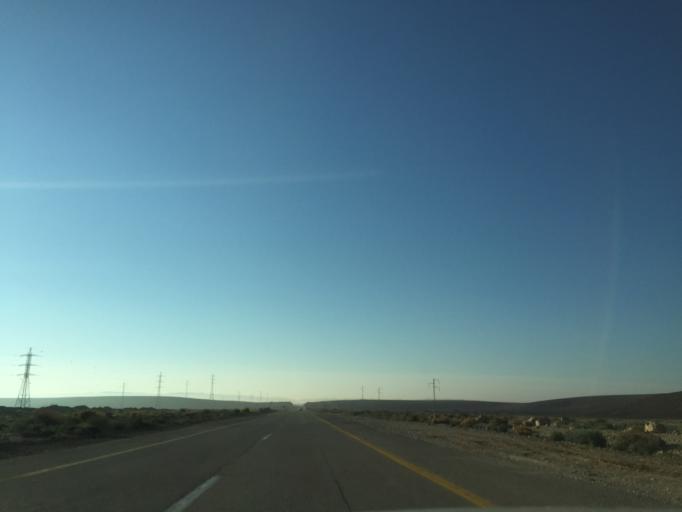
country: IL
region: Southern District
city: Mitzpe Ramon
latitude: 30.4687
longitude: 34.9332
